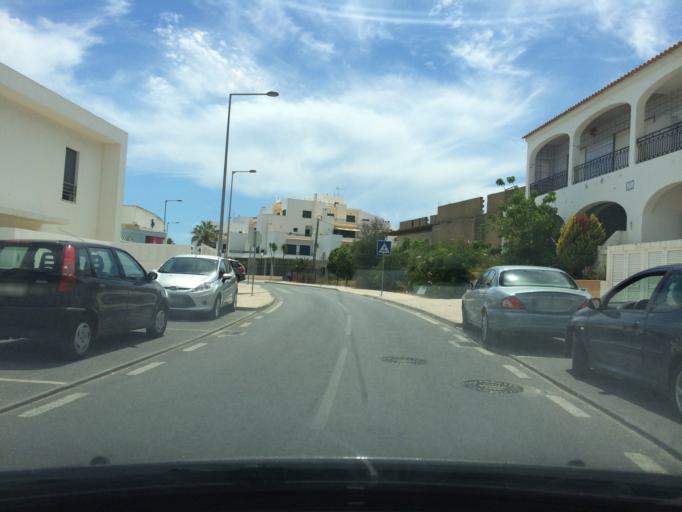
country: PT
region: Faro
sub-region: Albufeira
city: Albufeira
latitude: 37.0912
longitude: -8.1947
